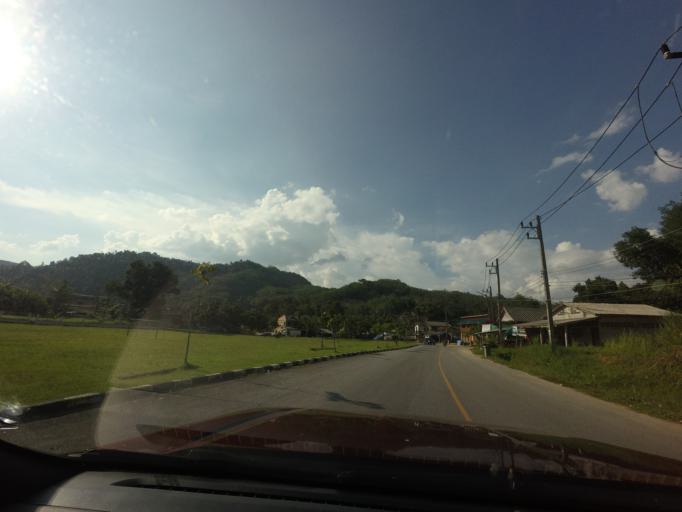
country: TH
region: Yala
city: Than To
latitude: 6.1592
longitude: 101.2787
